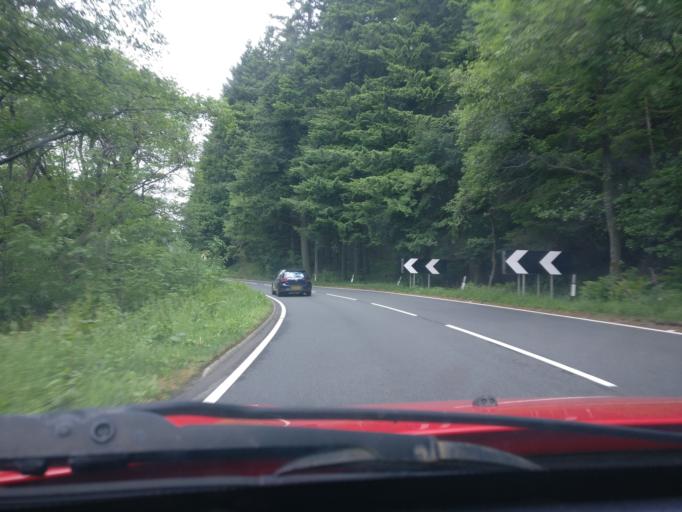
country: GB
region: Scotland
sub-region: Stirling
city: Callander
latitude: 56.2763
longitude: -4.2820
